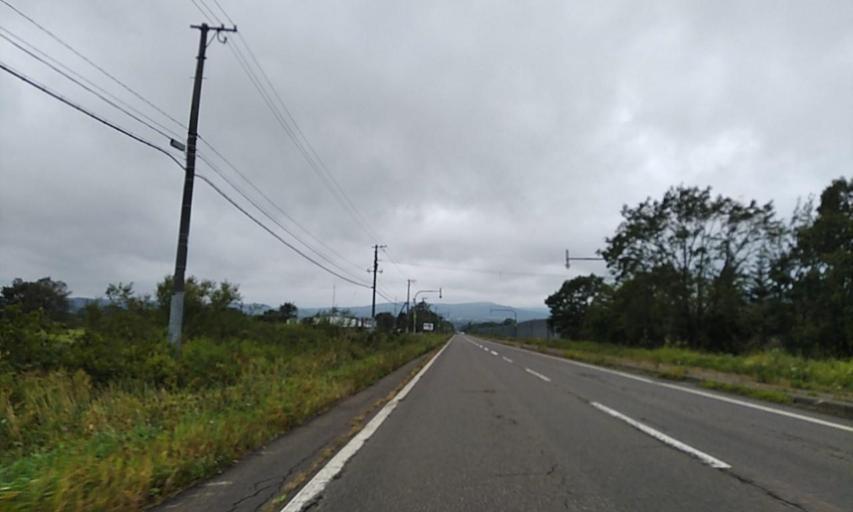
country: JP
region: Hokkaido
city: Bihoro
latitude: 43.5114
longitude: 144.4692
